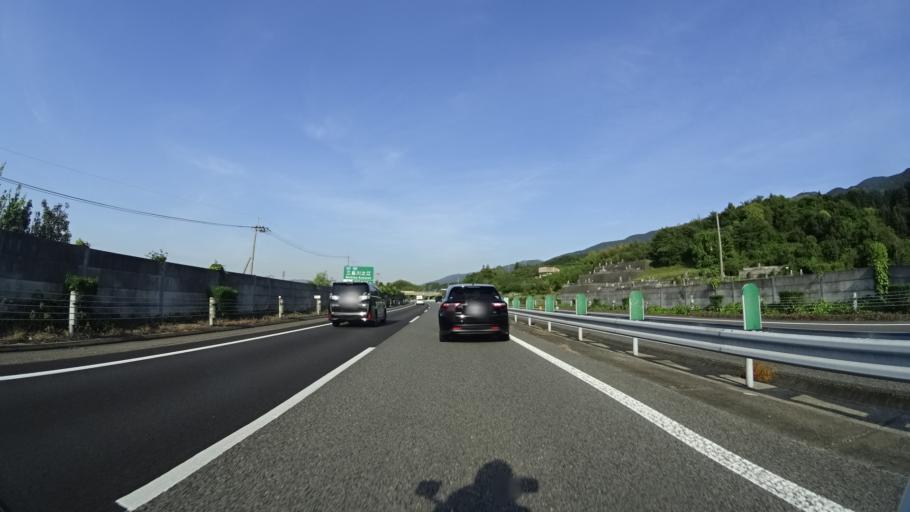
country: JP
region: Ehime
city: Kawanoecho
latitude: 33.9763
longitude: 133.5663
